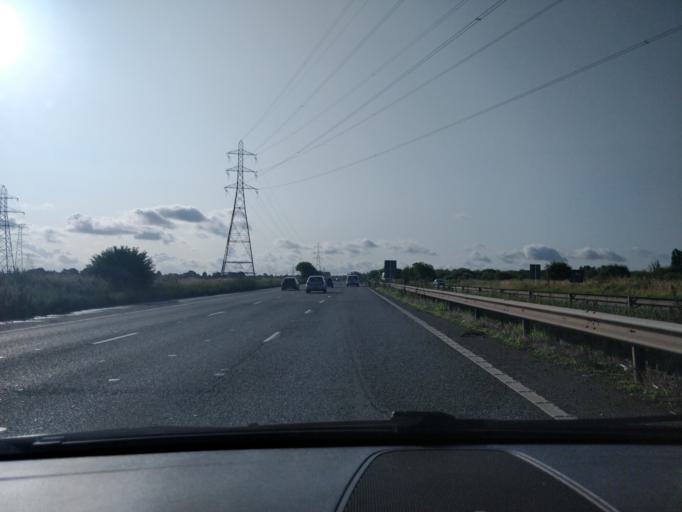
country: GB
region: England
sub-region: Sefton
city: Maghull
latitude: 53.4910
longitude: -2.9452
